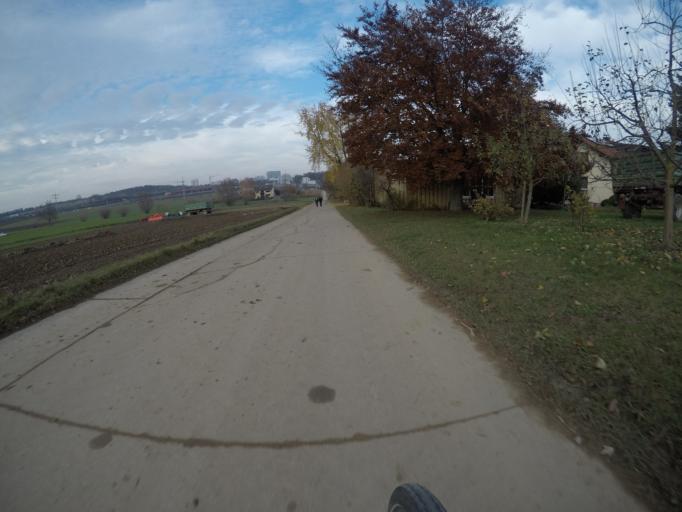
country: DE
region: Baden-Wuerttemberg
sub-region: Regierungsbezirk Stuttgart
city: Leinfelden-Echterdingen
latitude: 48.6998
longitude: 9.1734
